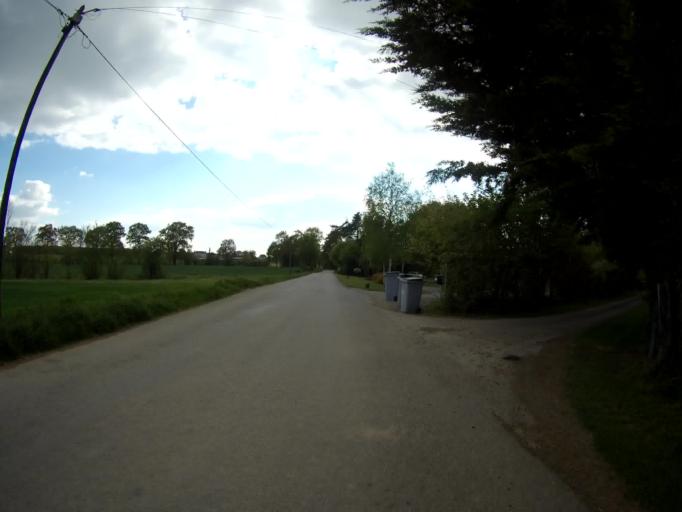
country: FR
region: Brittany
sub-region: Departement d'Ille-et-Vilaine
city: Vern-sur-Seiche
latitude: 48.0708
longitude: -1.5832
